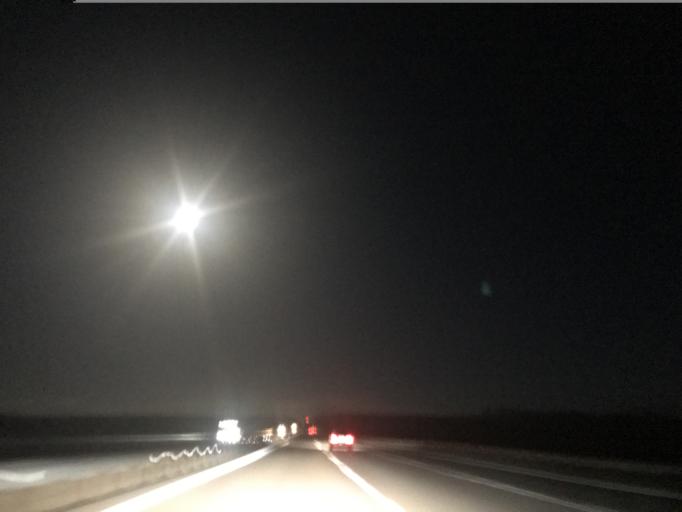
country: TR
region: Nigde
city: Ulukisla
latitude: 37.6395
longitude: 34.3884
